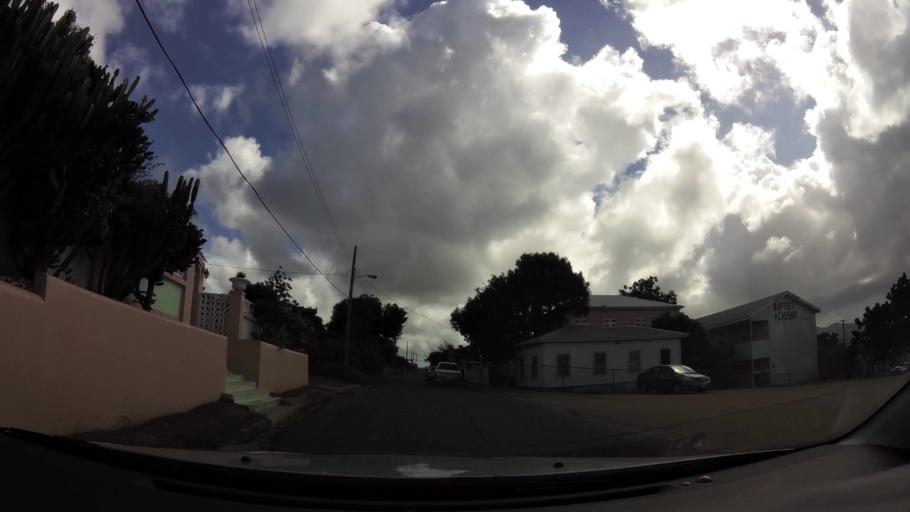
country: AG
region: Saint John
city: Saint John's
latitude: 17.1126
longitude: -61.8354
